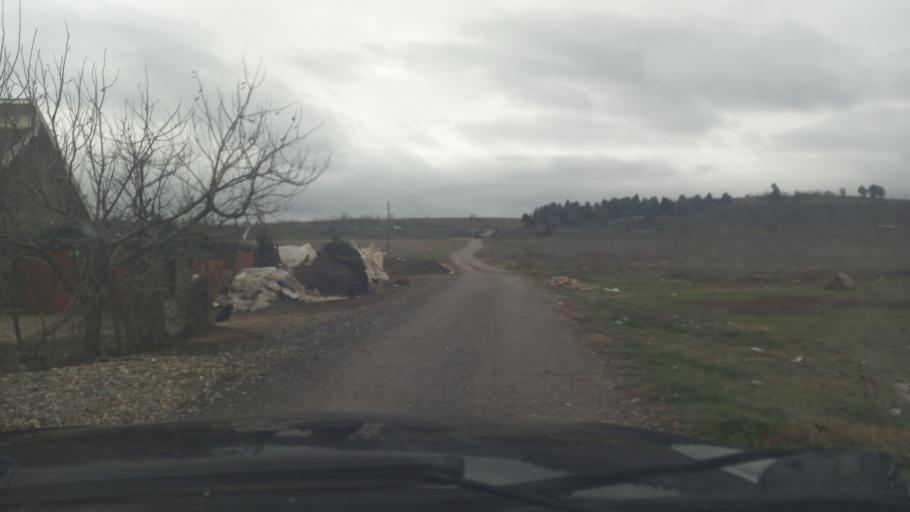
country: MK
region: Gradsko
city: Gradsko
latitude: 41.5787
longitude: 21.9352
